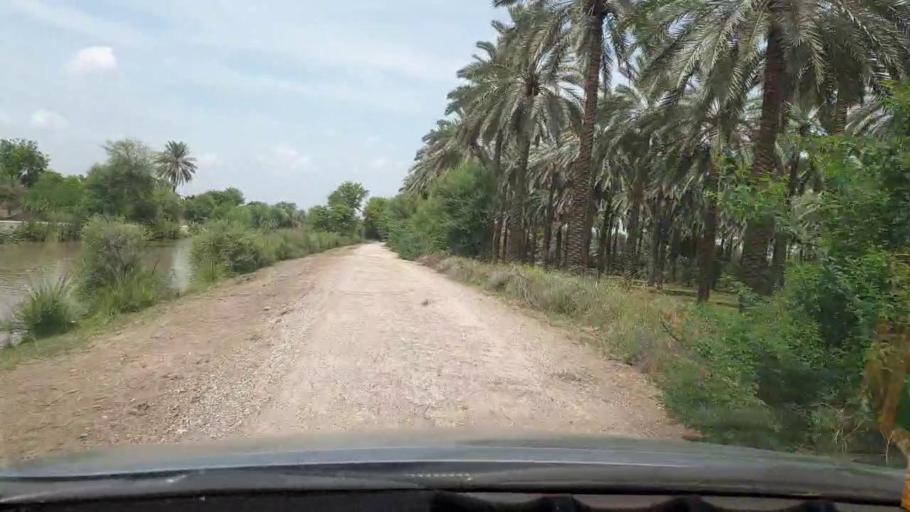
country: PK
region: Sindh
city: Khairpur
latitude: 27.4626
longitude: 68.8039
